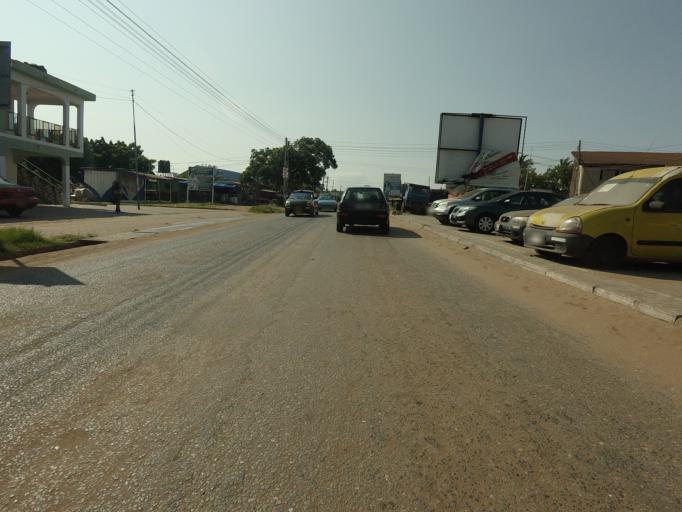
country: GH
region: Greater Accra
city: Teshi Old Town
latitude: 5.5893
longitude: -0.0990
